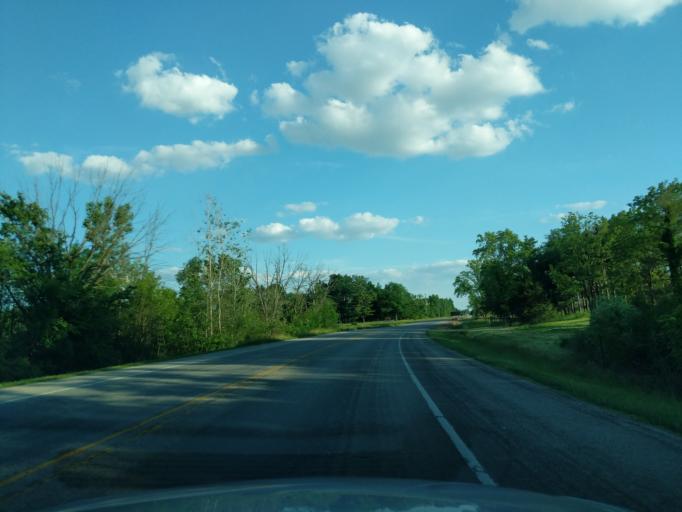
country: US
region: Indiana
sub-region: Huntington County
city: Huntington
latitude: 40.8391
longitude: -85.4656
